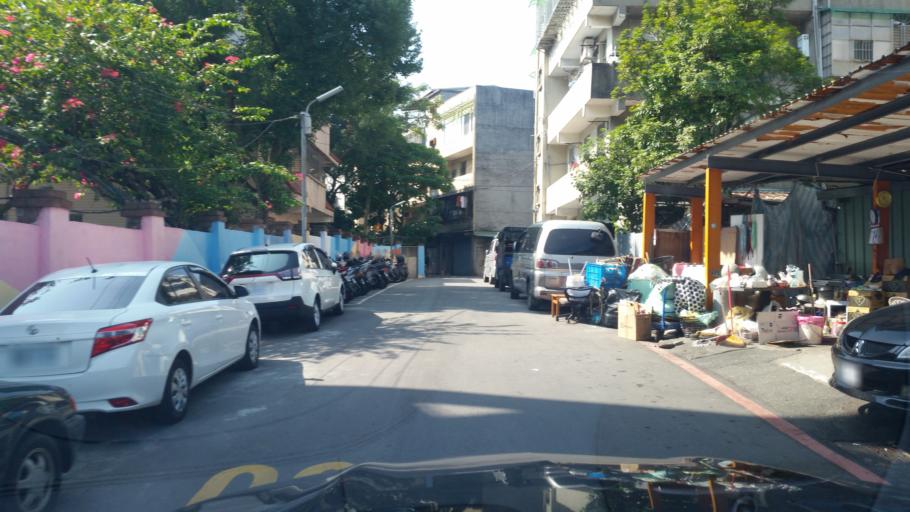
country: TW
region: Taipei
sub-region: Taipei
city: Banqiao
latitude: 24.9860
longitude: 121.5180
